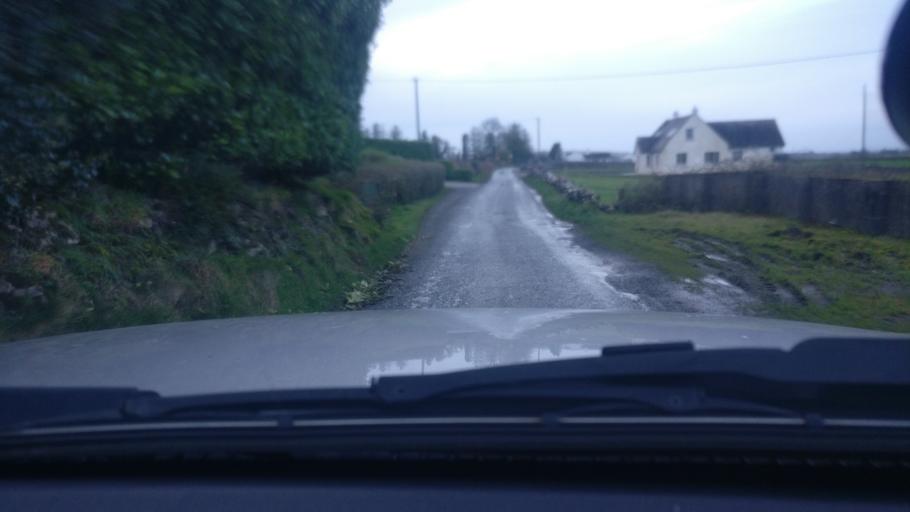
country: IE
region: Connaught
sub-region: County Galway
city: Loughrea
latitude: 53.1638
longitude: -8.5590
